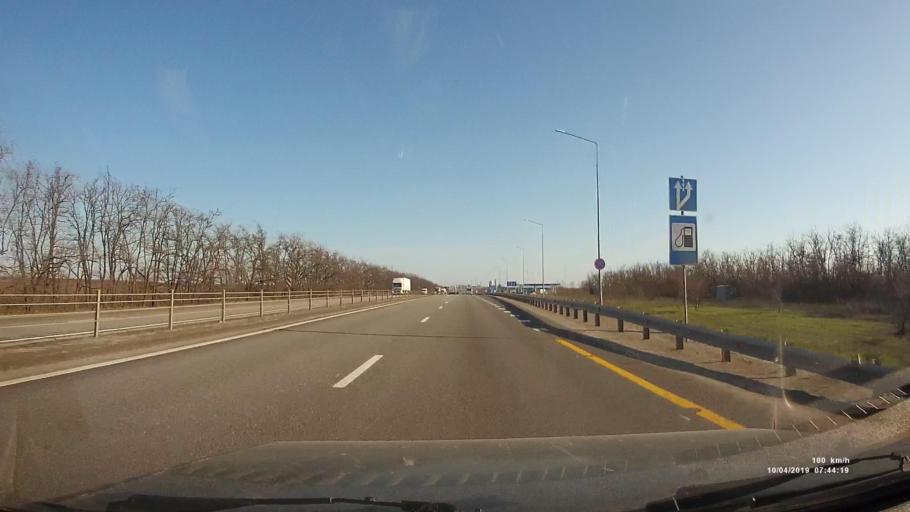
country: RU
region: Rostov
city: Likhoy
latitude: 48.1761
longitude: 40.2644
